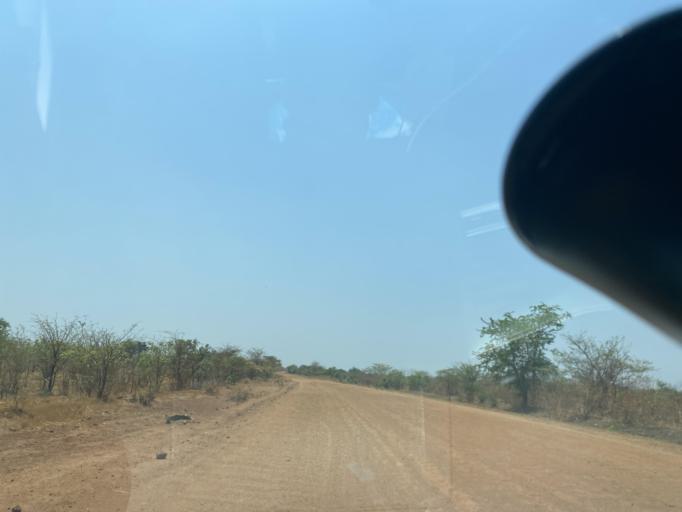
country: ZM
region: Lusaka
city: Lusaka
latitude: -15.4606
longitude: 27.9265
